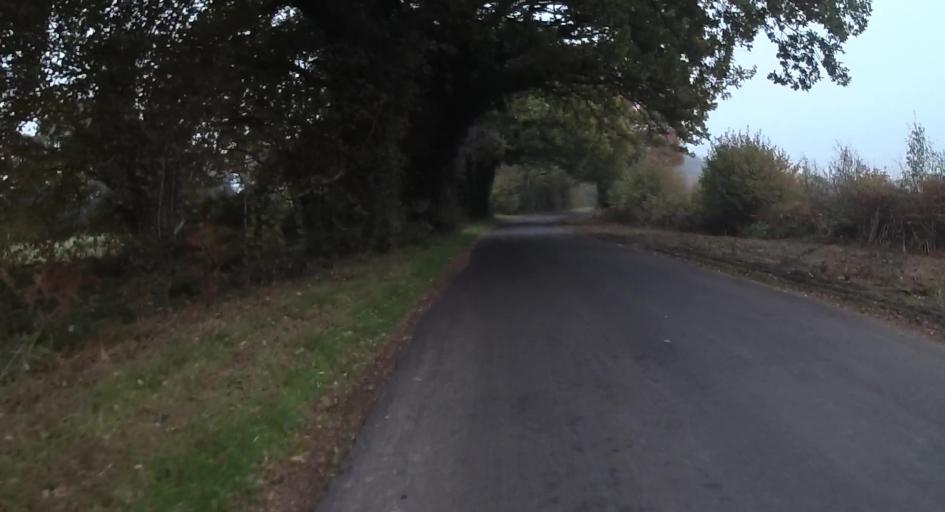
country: GB
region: England
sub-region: Hampshire
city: Long Sutton
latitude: 51.1996
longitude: -0.9444
